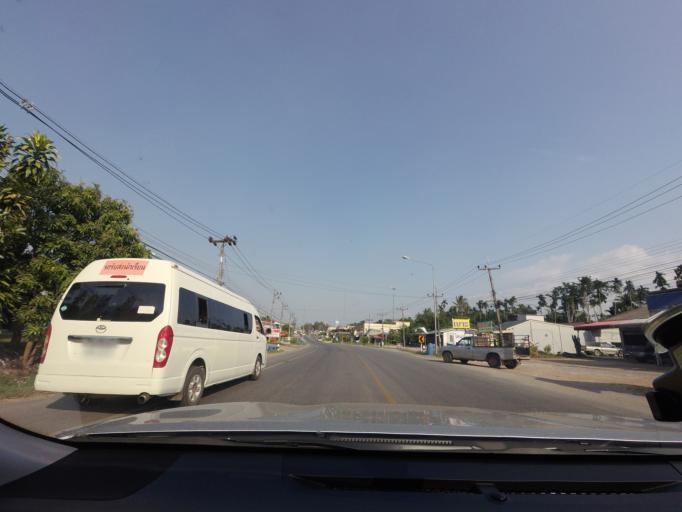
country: TH
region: Surat Thani
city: Phrasaeng
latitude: 8.5728
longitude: 99.2248
